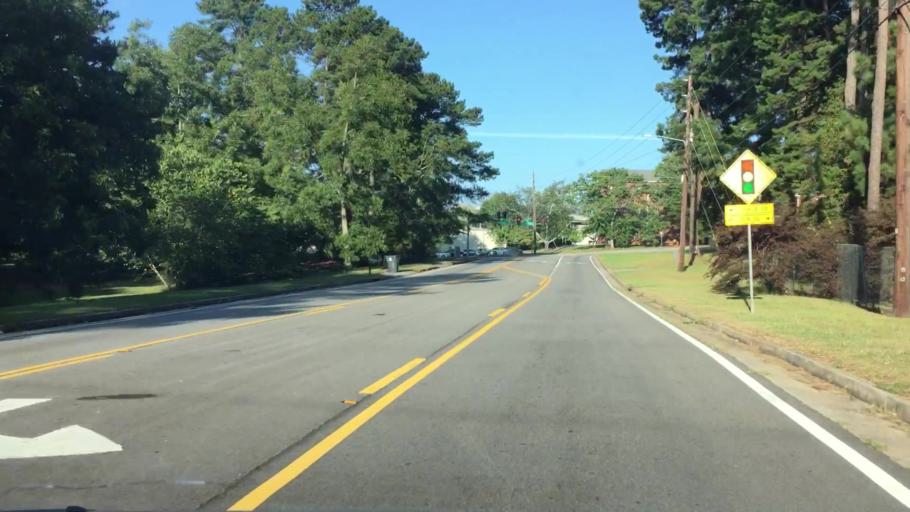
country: US
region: Georgia
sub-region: Clayton County
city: Morrow
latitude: 33.5601
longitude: -84.3203
